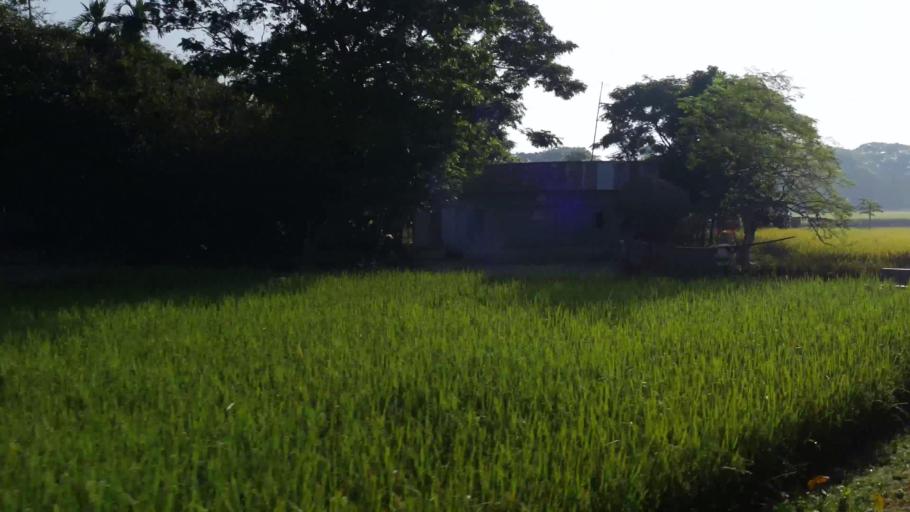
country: BD
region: Dhaka
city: Jamalpur
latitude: 24.8632
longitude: 90.0634
